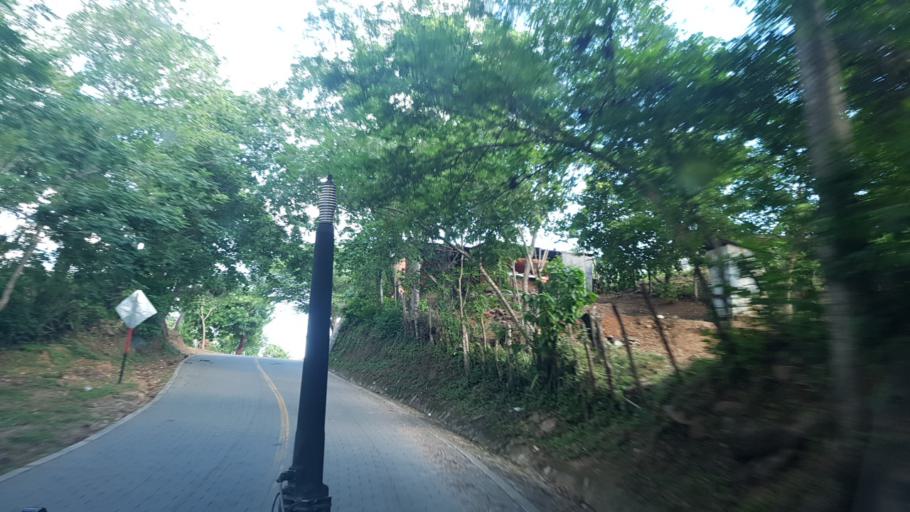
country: NI
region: Nueva Segovia
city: Ocotal
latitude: 13.6510
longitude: -86.6115
